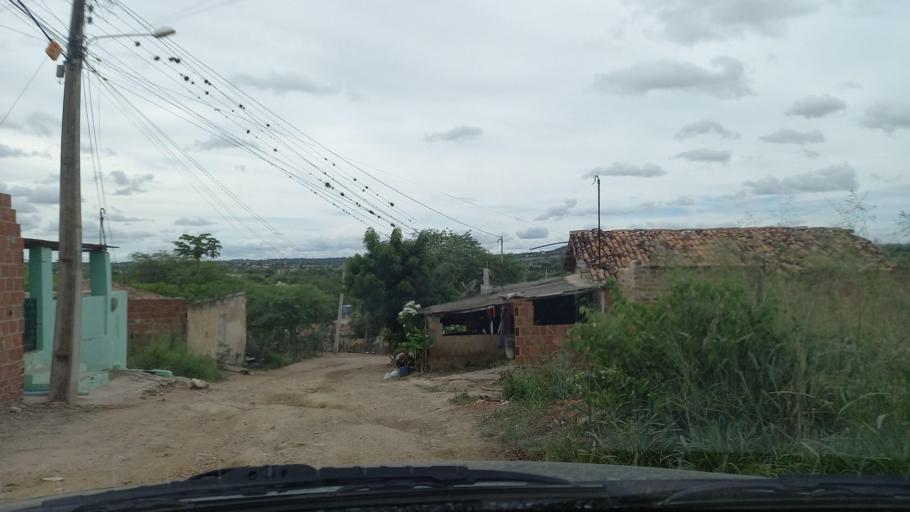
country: BR
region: Pernambuco
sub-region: Gravata
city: Gravata
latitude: -8.2149
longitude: -35.6085
